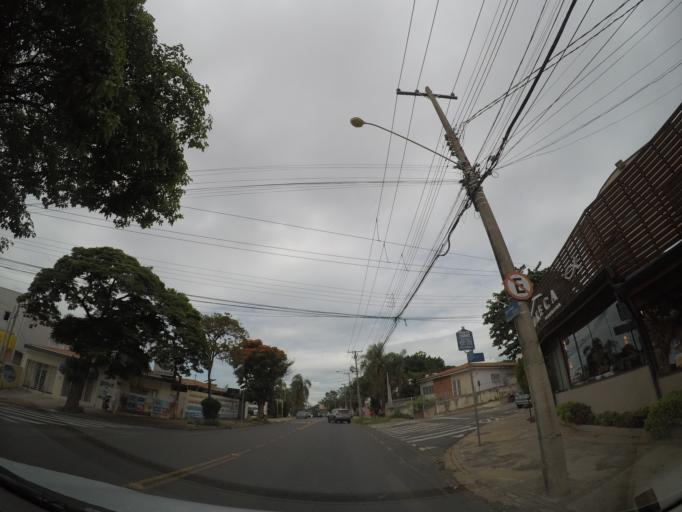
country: BR
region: Sao Paulo
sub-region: Campinas
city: Campinas
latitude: -22.8840
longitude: -47.0362
